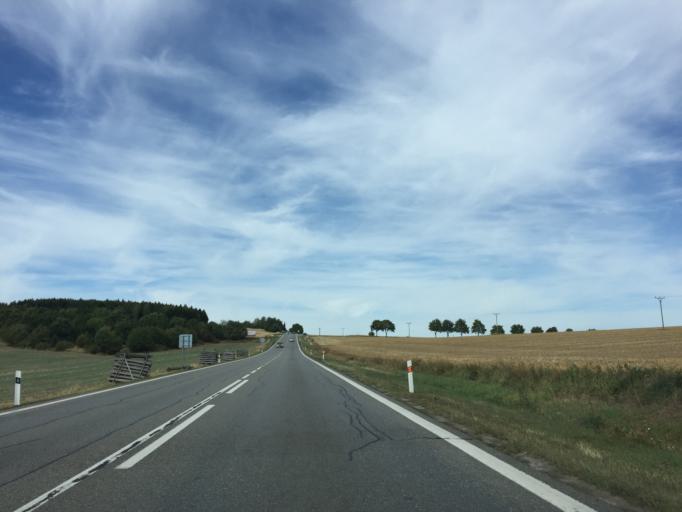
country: CZ
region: Jihocesky
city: Chotoviny
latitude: 49.5489
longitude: 14.6650
